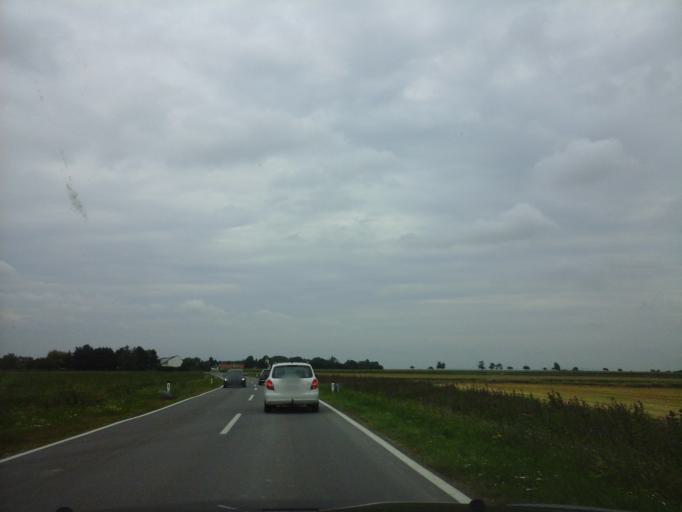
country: AT
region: Lower Austria
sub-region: Politischer Bezirk Ganserndorf
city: Haringsee
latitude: 48.1647
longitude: 16.7650
